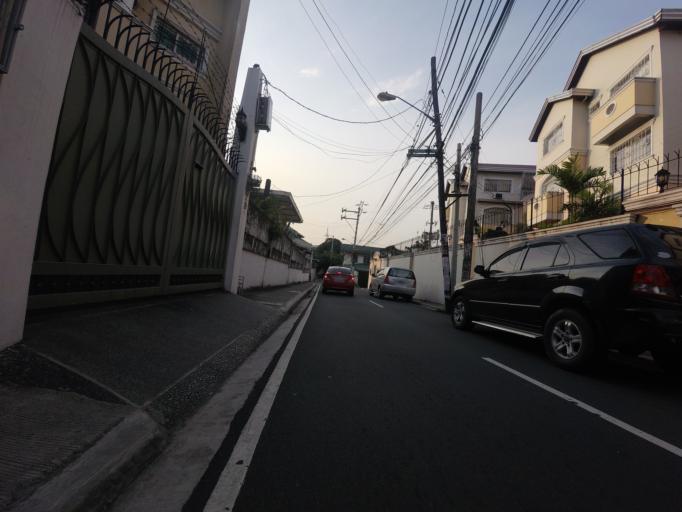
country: PH
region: Metro Manila
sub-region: San Juan
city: San Juan
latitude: 14.6085
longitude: 121.0269
